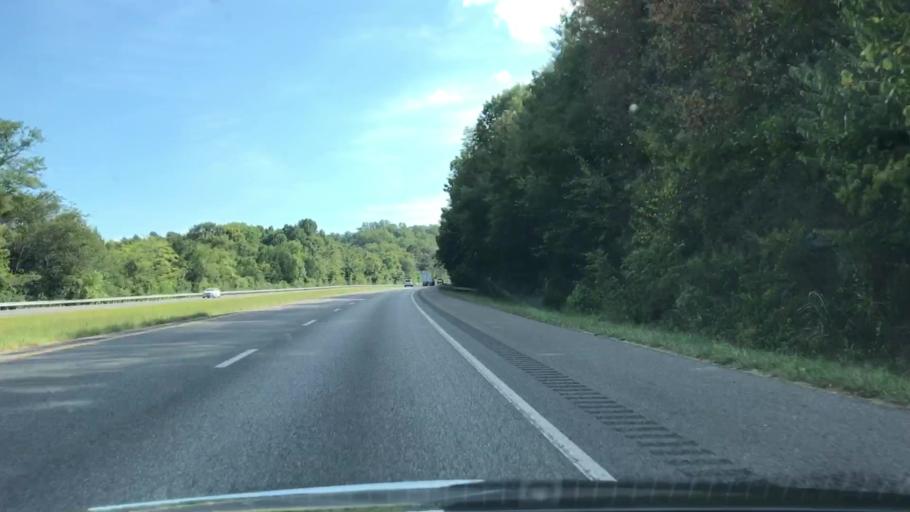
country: US
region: Alabama
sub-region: Limestone County
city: Ardmore
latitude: 35.1245
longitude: -86.8775
